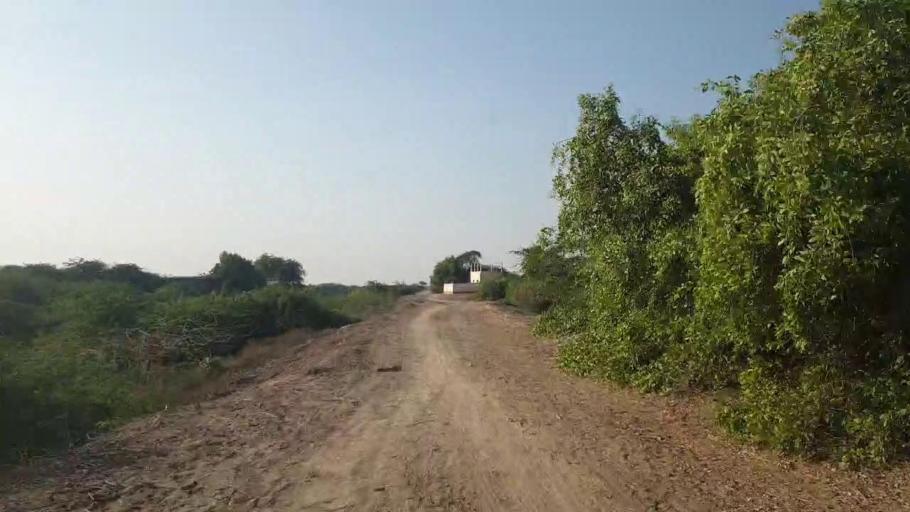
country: PK
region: Sindh
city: Badin
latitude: 24.4700
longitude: 68.7401
